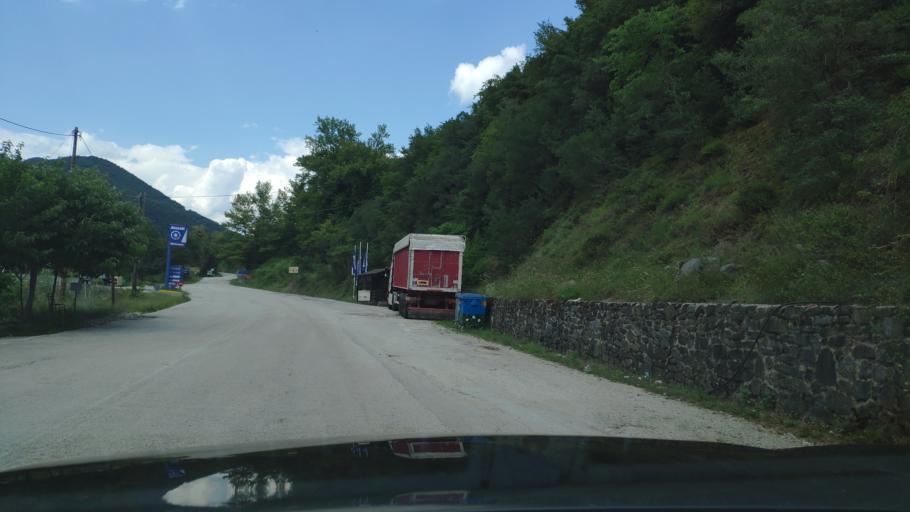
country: GR
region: Epirus
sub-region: Nomos Artas
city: Agios Dimitrios
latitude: 39.4552
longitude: 21.0344
